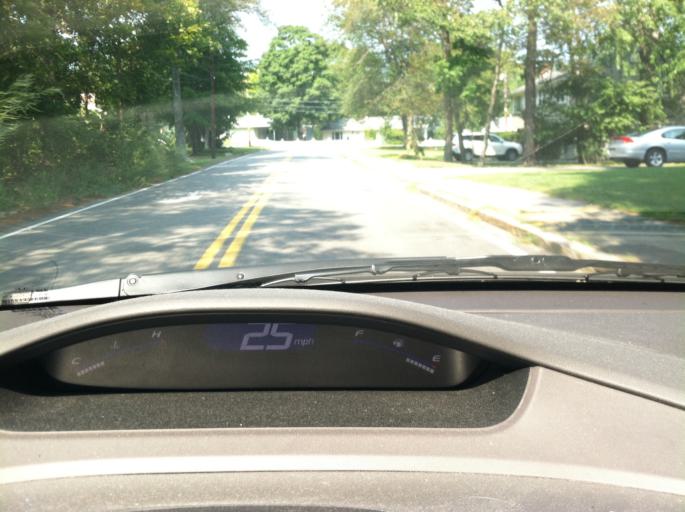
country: US
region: Massachusetts
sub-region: Middlesex County
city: Bedford
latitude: 42.4992
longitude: -71.2770
